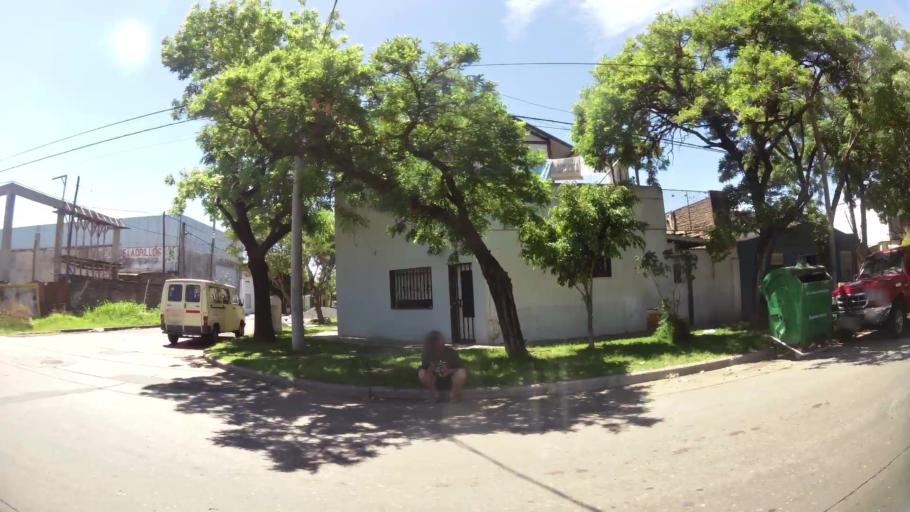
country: AR
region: Santa Fe
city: Perez
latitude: -32.9416
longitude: -60.7218
